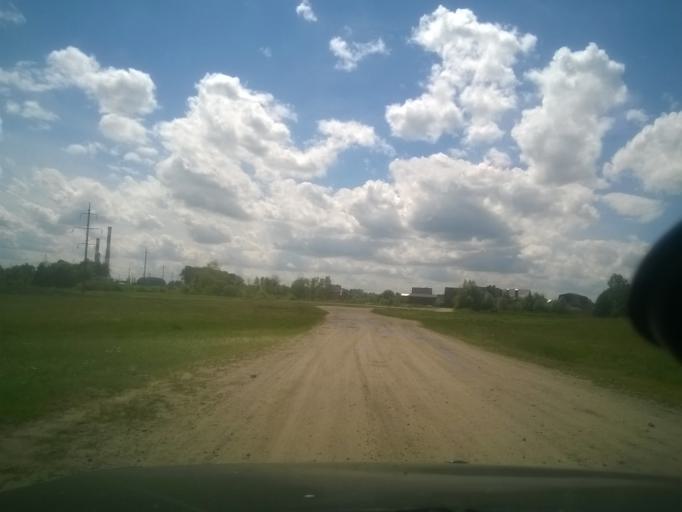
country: RU
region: Kursk
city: Kursk
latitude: 51.6804
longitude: 36.1139
